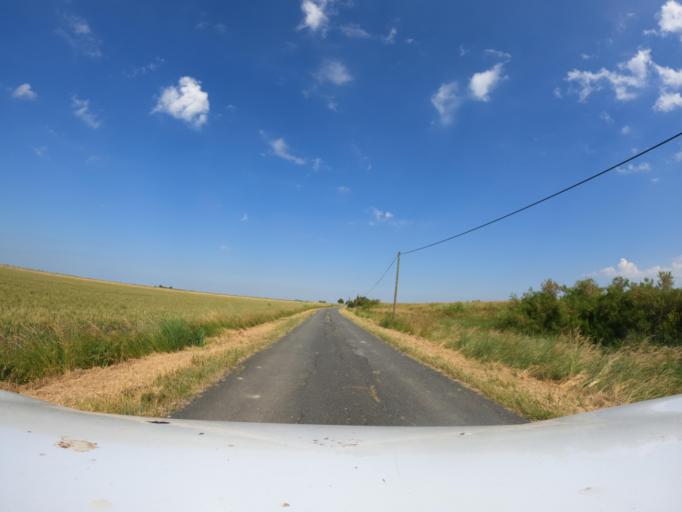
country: FR
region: Poitou-Charentes
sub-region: Departement de la Charente-Maritime
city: Charron
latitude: 46.3291
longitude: -1.1560
